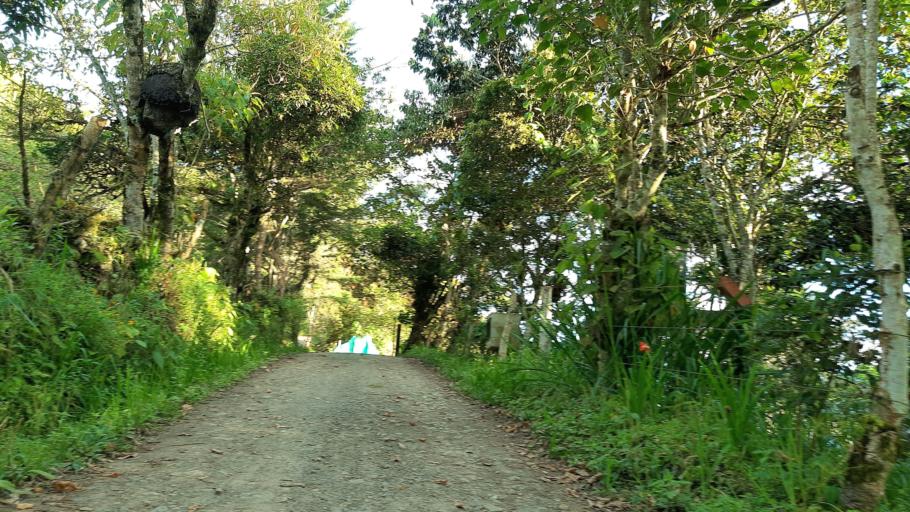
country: CO
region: Boyaca
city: Garagoa
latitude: 5.0628
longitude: -73.3773
